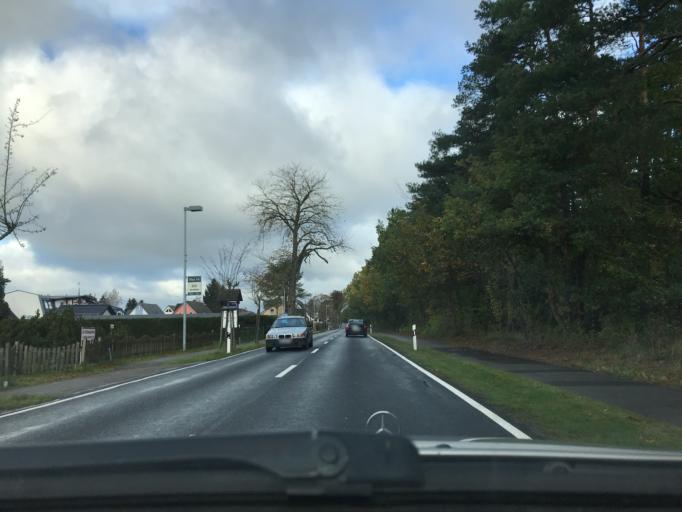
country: DE
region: Mecklenburg-Vorpommern
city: Karlshagen
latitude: 54.1087
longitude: 13.8411
